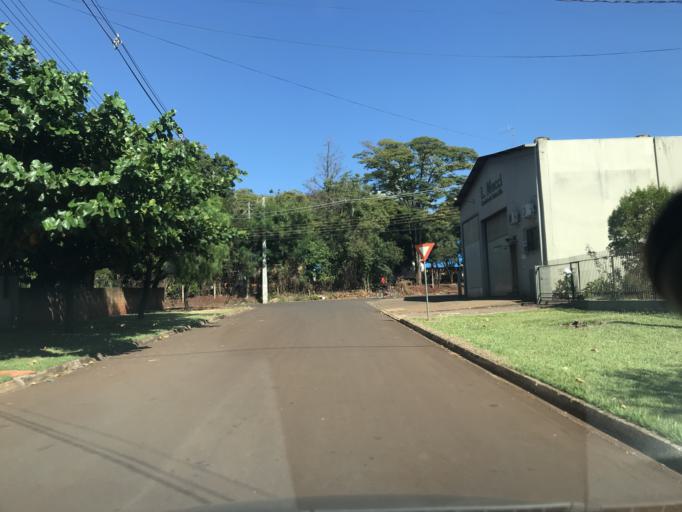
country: BR
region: Parana
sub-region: Palotina
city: Palotina
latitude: -24.2786
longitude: -53.8275
